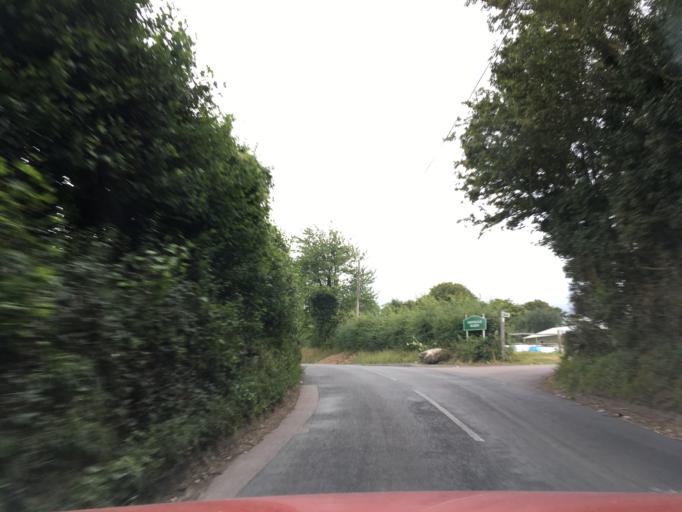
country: GB
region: England
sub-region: Kent
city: Yalding
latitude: 51.2386
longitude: 0.4480
